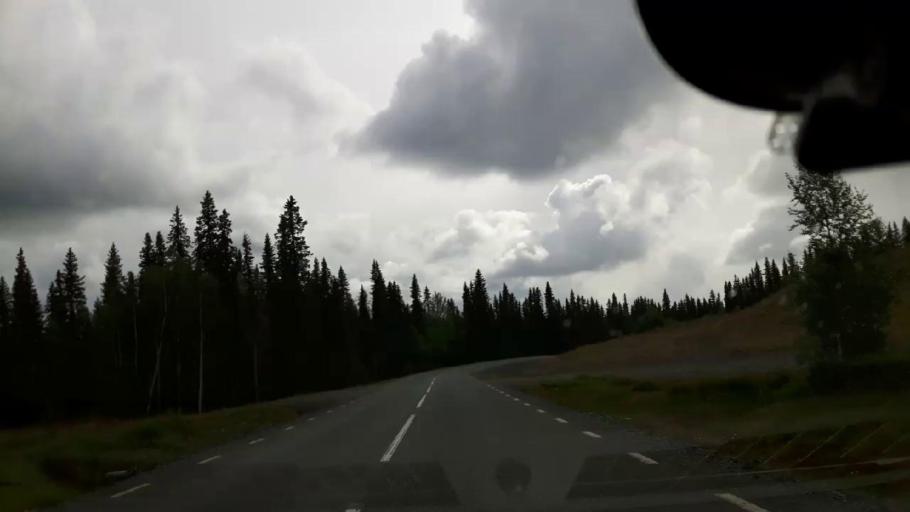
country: SE
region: Jaemtland
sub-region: Krokoms Kommun
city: Valla
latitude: 63.4466
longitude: 13.8295
